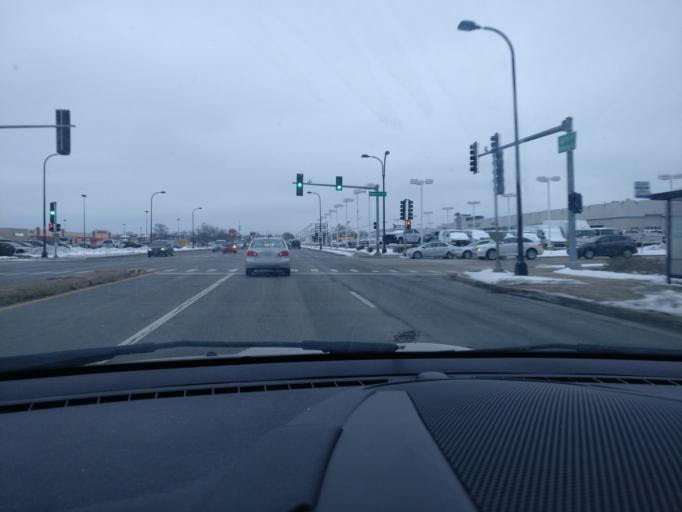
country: US
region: Illinois
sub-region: Cook County
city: Park Ridge
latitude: 42.0398
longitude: -87.8459
